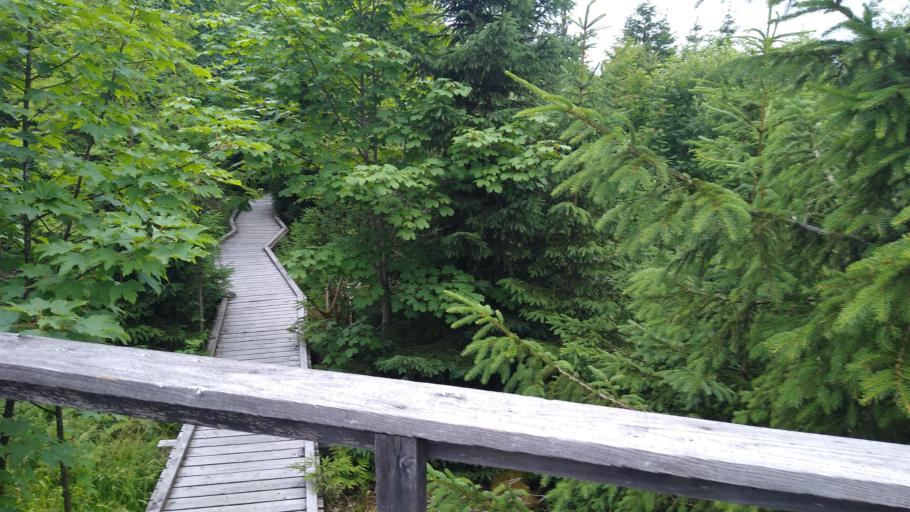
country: DE
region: North Rhine-Westphalia
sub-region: Regierungsbezirk Arnsberg
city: Bad Berleburg
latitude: 51.1290
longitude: 8.3793
